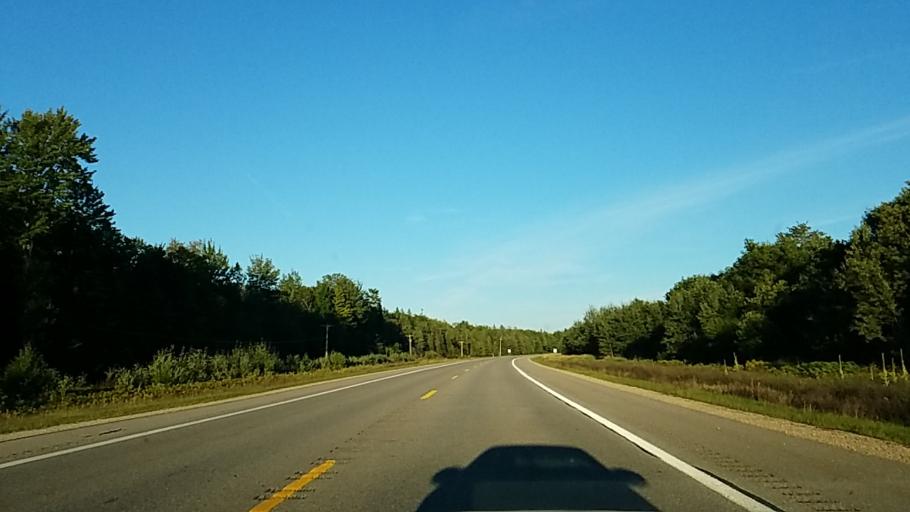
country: US
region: Michigan
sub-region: Alger County
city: Munising
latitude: 46.4425
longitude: -86.7359
